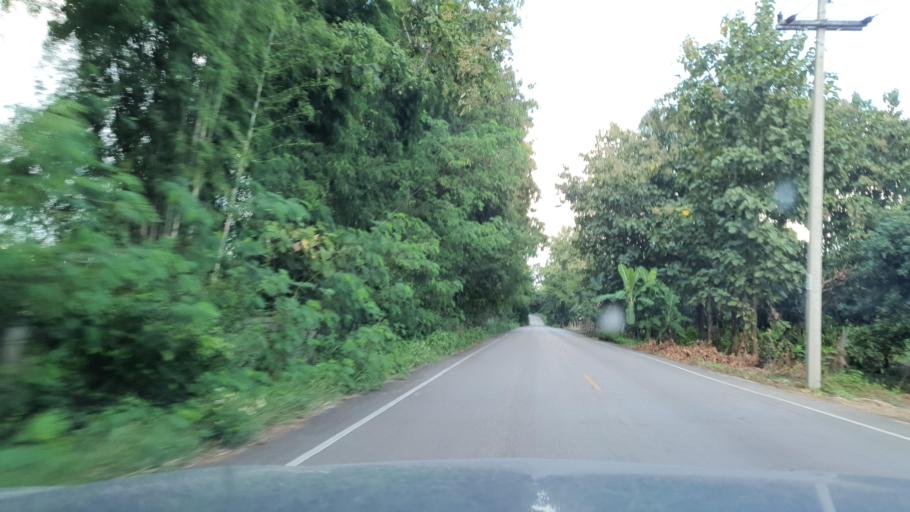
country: TH
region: Phayao
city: Phayao
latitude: 19.0939
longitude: 99.8293
